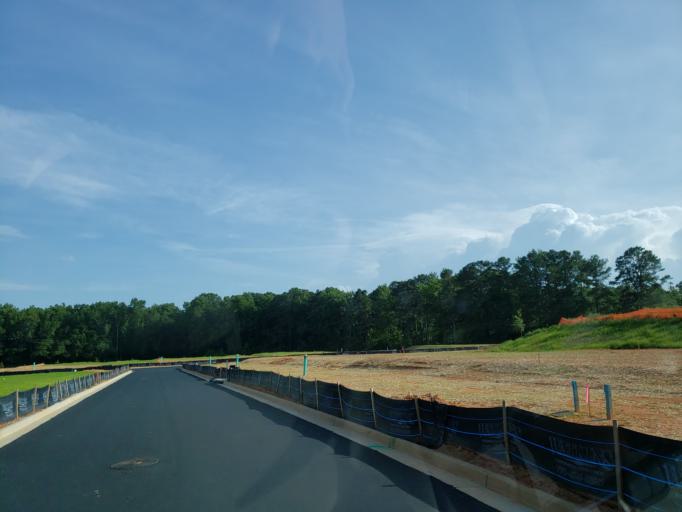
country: US
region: Georgia
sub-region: Cobb County
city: Powder Springs
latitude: 33.9095
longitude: -84.7032
